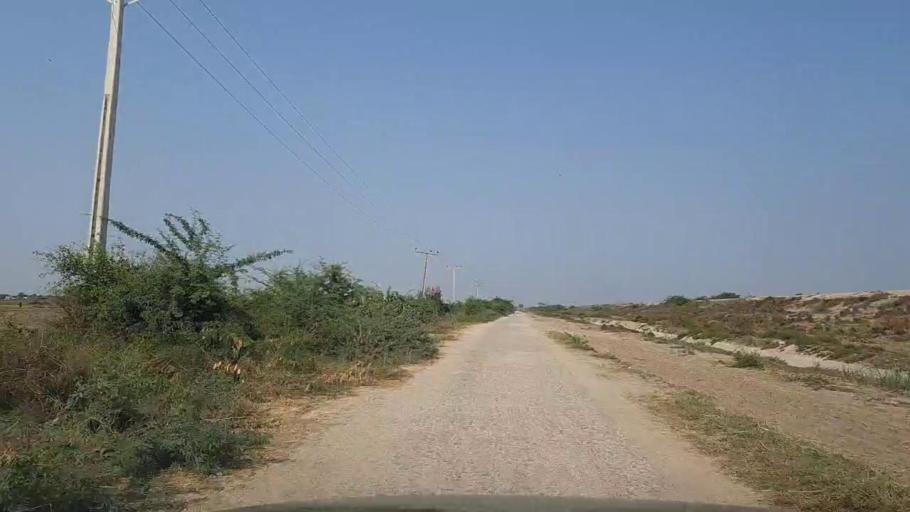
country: PK
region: Sindh
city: Chuhar Jamali
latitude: 24.5160
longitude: 67.9252
